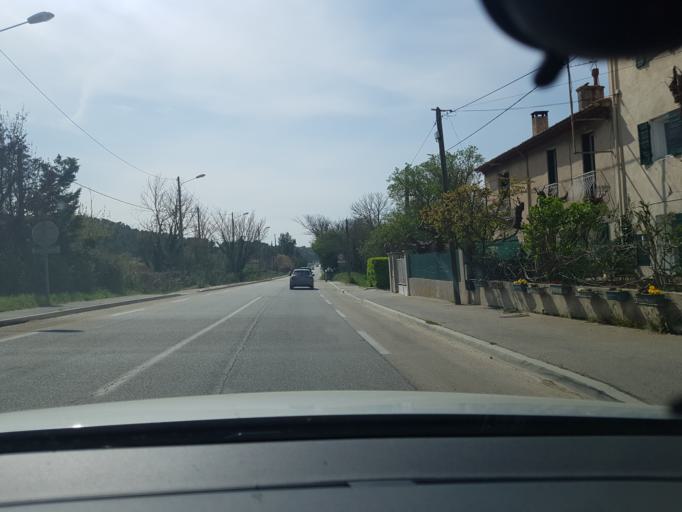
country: FR
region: Provence-Alpes-Cote d'Azur
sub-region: Departement des Bouches-du-Rhone
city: Bouc-Bel-Air
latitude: 43.4748
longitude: 5.4132
